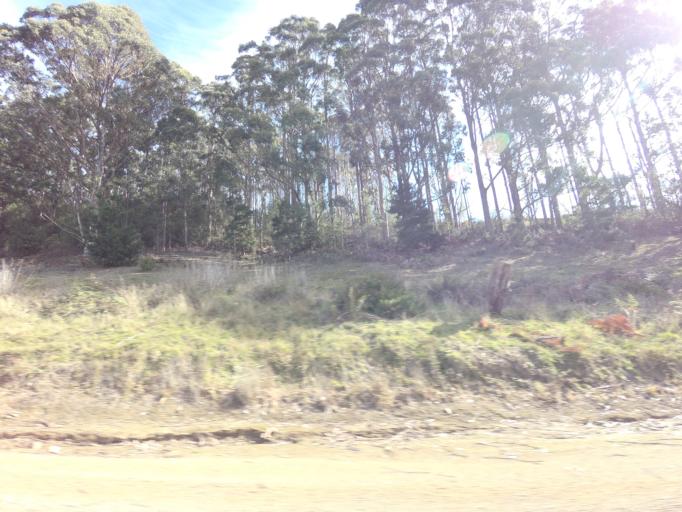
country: AU
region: Tasmania
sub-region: Clarence
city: Sandford
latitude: -43.1761
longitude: 147.7708
